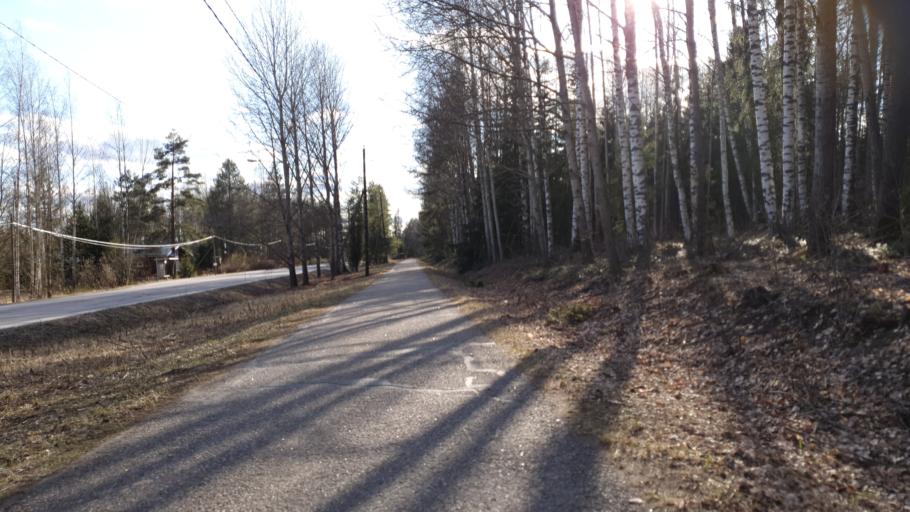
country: FI
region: Uusimaa
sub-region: Helsinki
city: Tuusula
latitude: 60.4061
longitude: 24.9456
